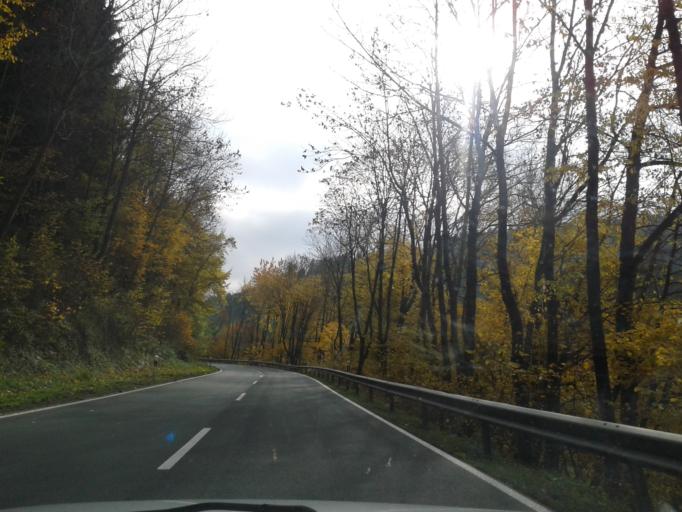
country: DE
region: North Rhine-Westphalia
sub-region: Regierungsbezirk Arnsberg
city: Bad Laasphe
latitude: 50.9633
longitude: 8.3484
